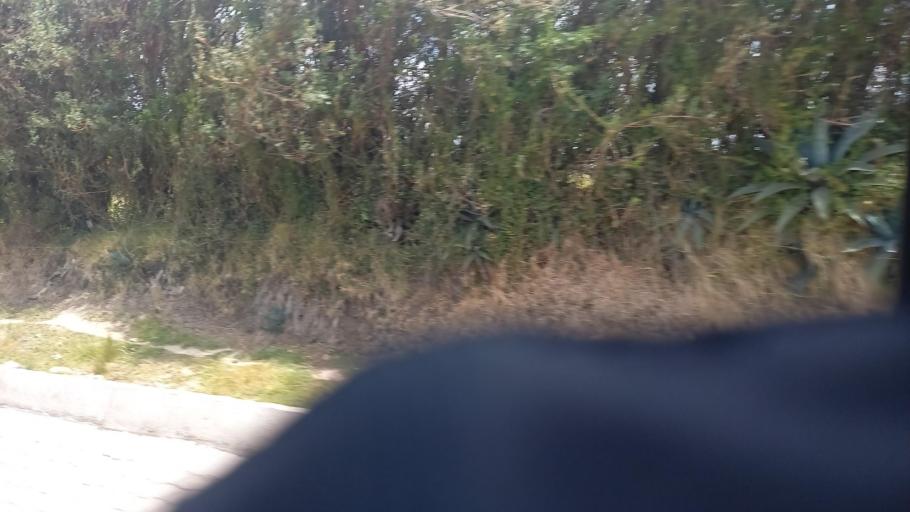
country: EC
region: Pichincha
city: Cayambe
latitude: 0.1588
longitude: -78.0748
